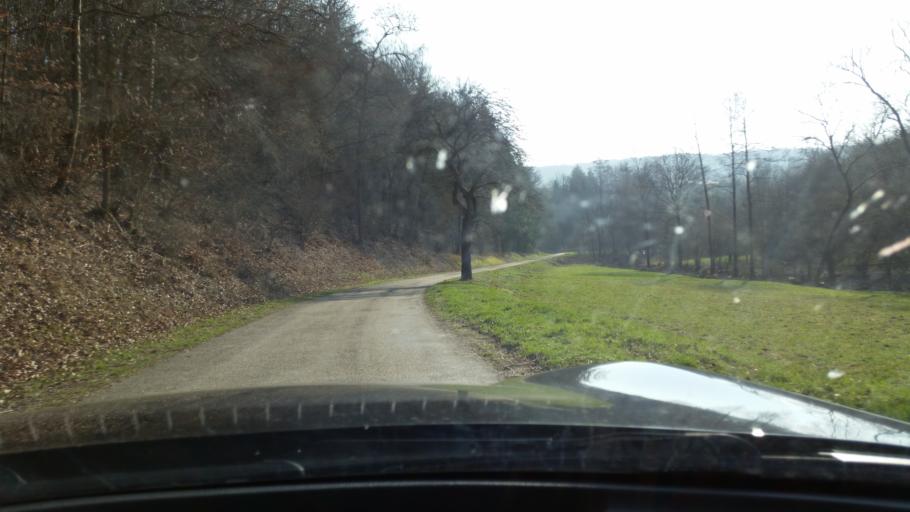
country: DE
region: Baden-Wuerttemberg
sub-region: Regierungsbezirk Stuttgart
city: Widdern
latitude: 49.3193
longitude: 9.3913
